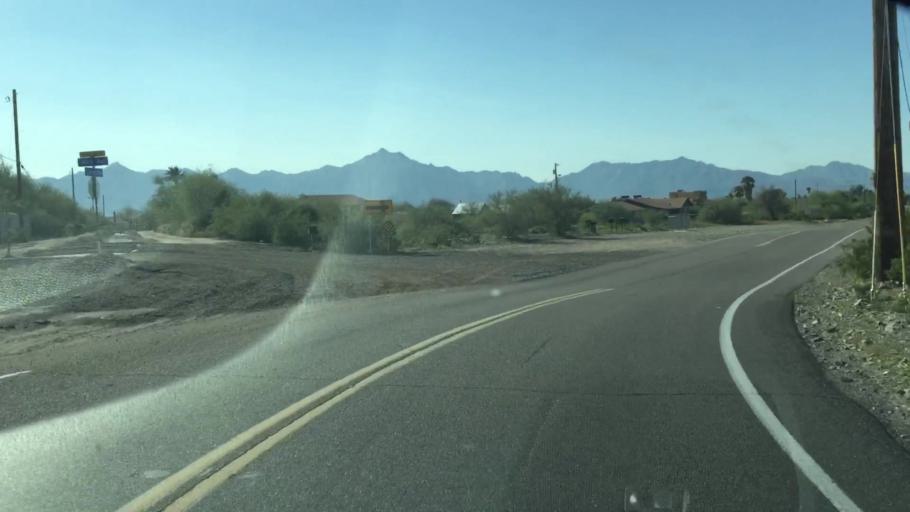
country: US
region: Arizona
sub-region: Maricopa County
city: Laveen
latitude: 33.3414
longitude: -112.1456
